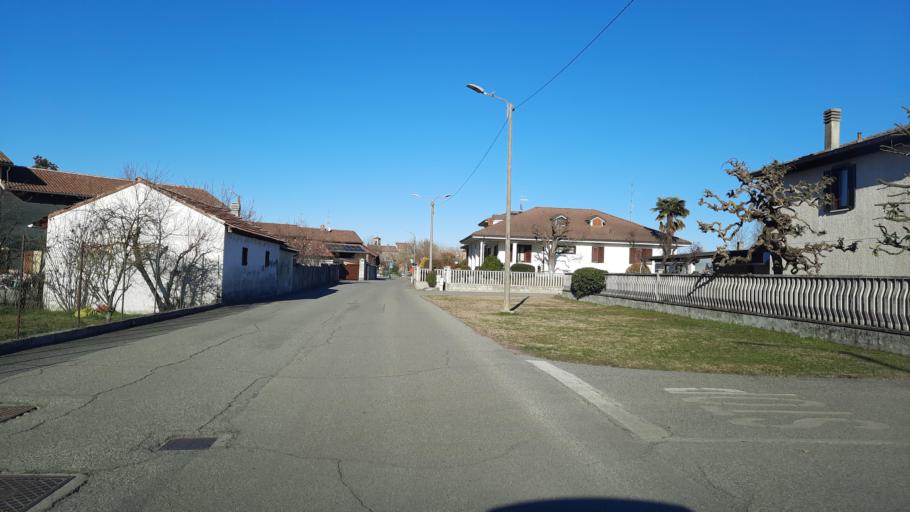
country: IT
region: Piedmont
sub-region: Provincia di Alessandria
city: Villanova Monferrato
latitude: 45.1786
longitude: 8.4753
